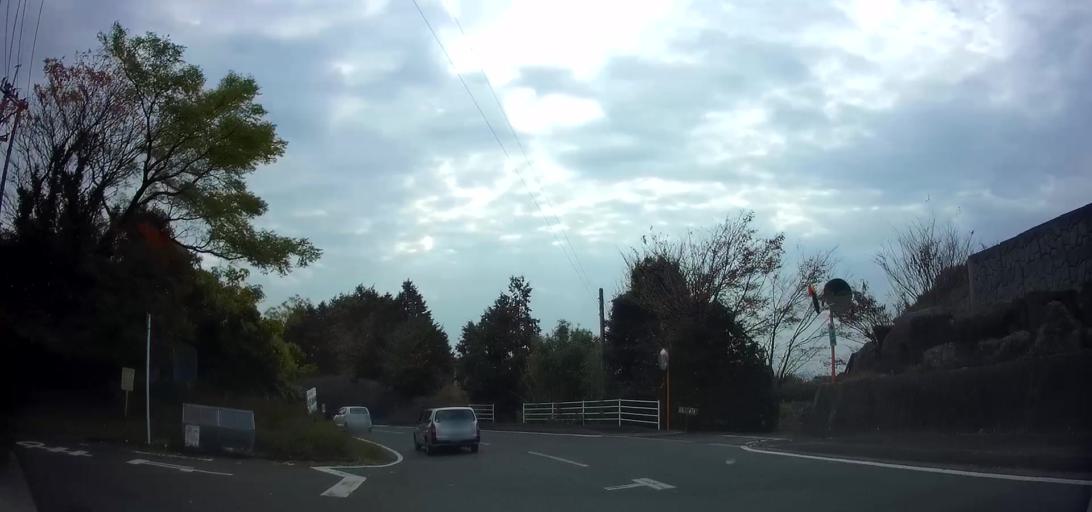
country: JP
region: Nagasaki
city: Shimabara
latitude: 32.6911
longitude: 130.3120
